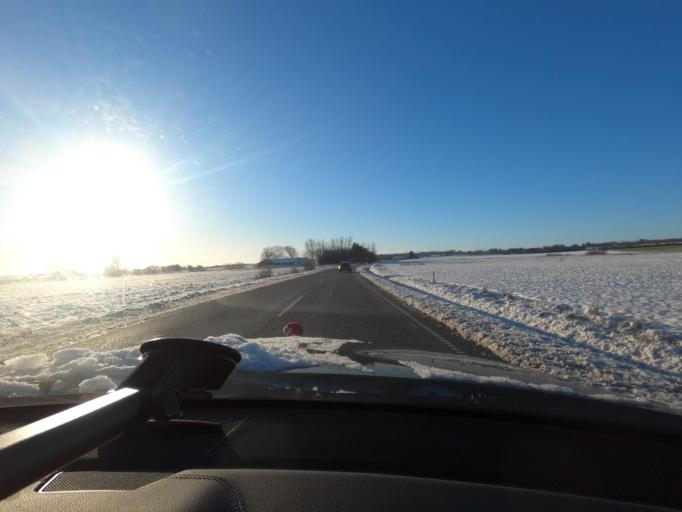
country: DK
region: South Denmark
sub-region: Tonder Kommune
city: Toftlund
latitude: 55.1711
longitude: 8.9874
